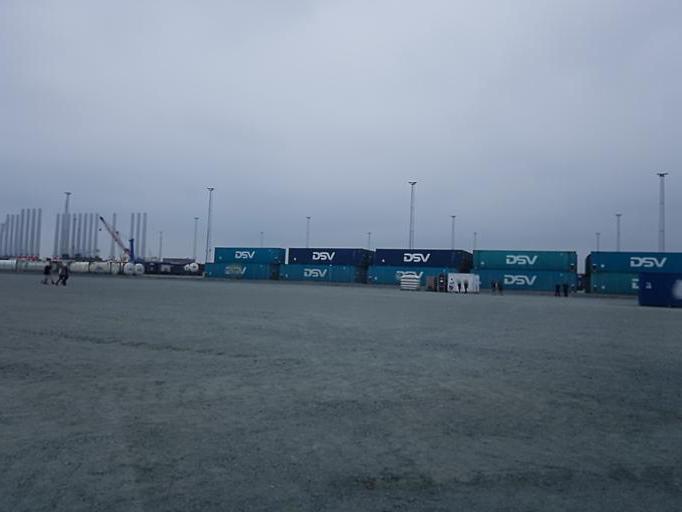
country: DK
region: South Denmark
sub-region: Esbjerg Kommune
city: Esbjerg
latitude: 55.4513
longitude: 8.4895
